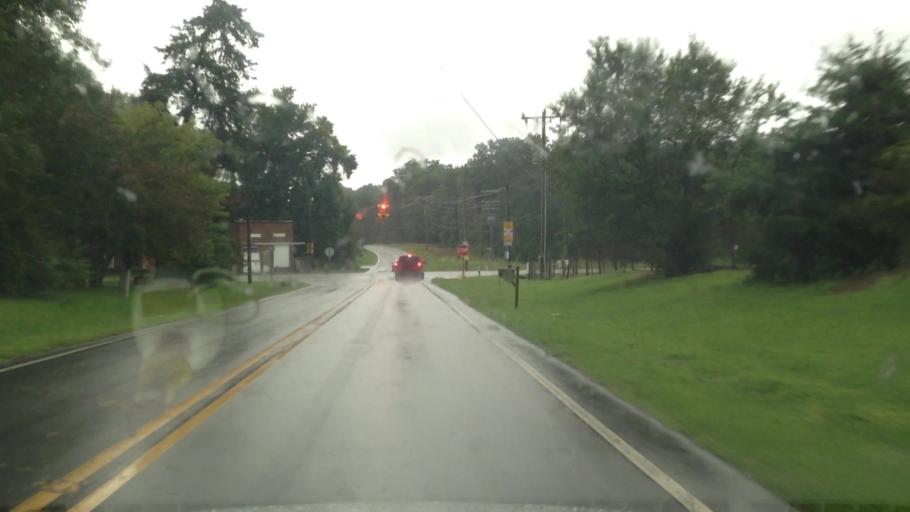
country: US
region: North Carolina
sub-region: Rockingham County
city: Reidsville
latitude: 36.2889
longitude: -79.7351
